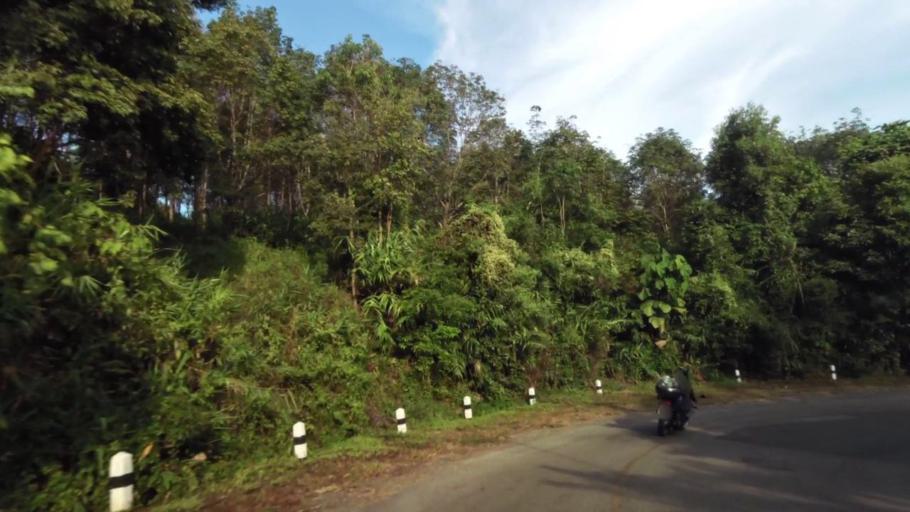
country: TH
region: Chiang Rai
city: Khun Tan
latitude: 19.8525
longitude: 100.3795
